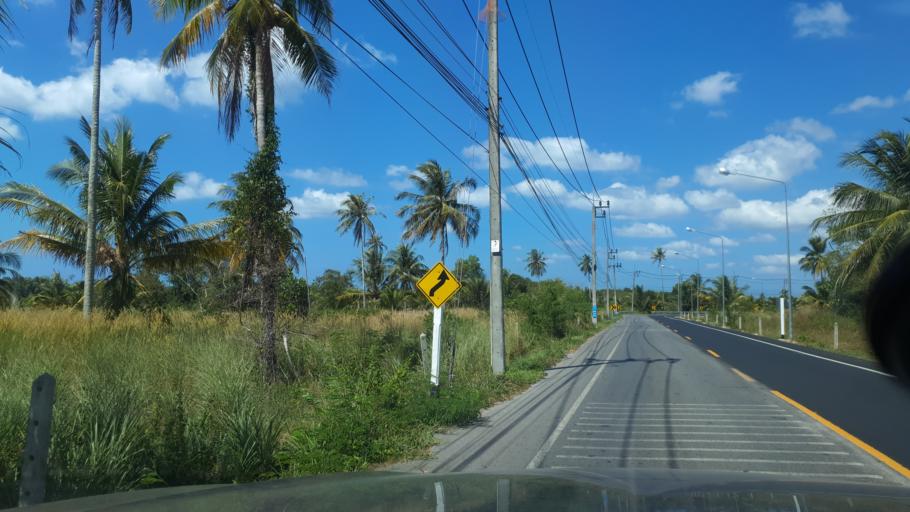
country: TH
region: Phuket
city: Thalang
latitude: 8.1432
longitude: 98.3064
